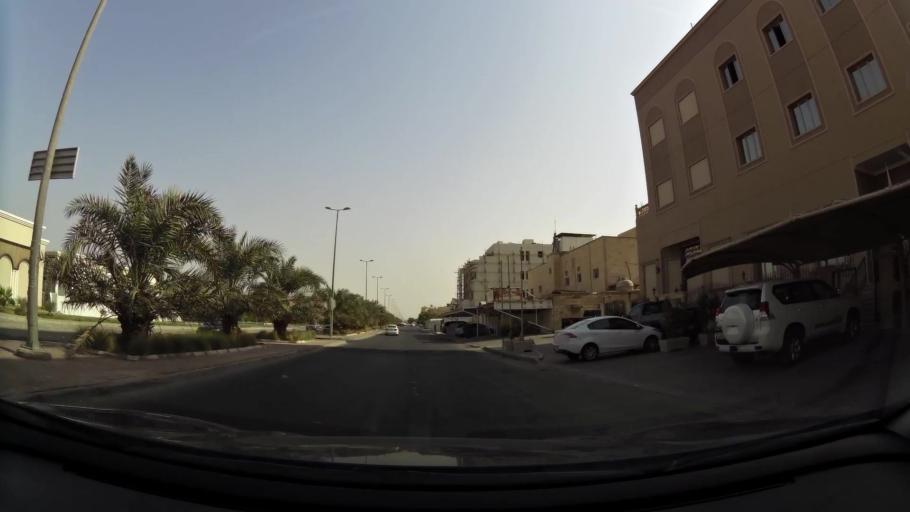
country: KW
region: Muhafazat al Jahra'
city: Al Jahra'
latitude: 29.3590
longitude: 47.6732
